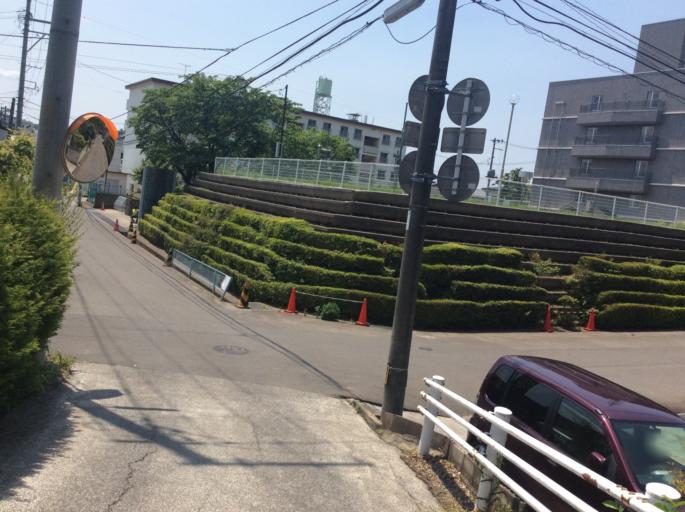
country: JP
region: Fukushima
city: Sukagawa
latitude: 37.1324
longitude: 140.2161
